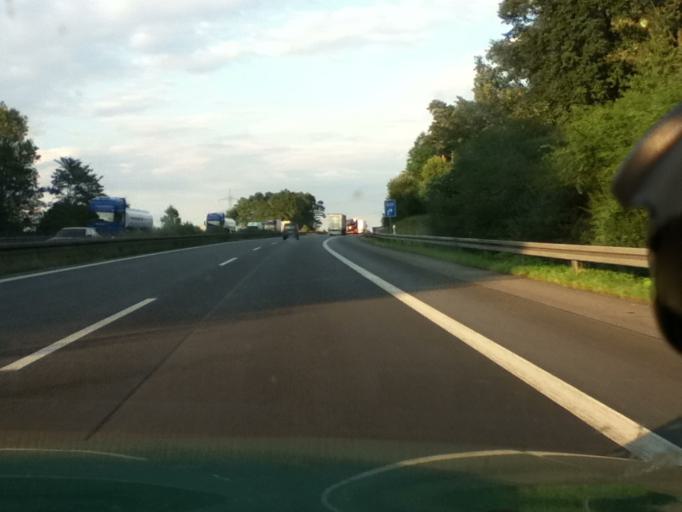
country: DE
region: Saxony
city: Burkau
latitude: 51.1964
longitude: 14.2083
